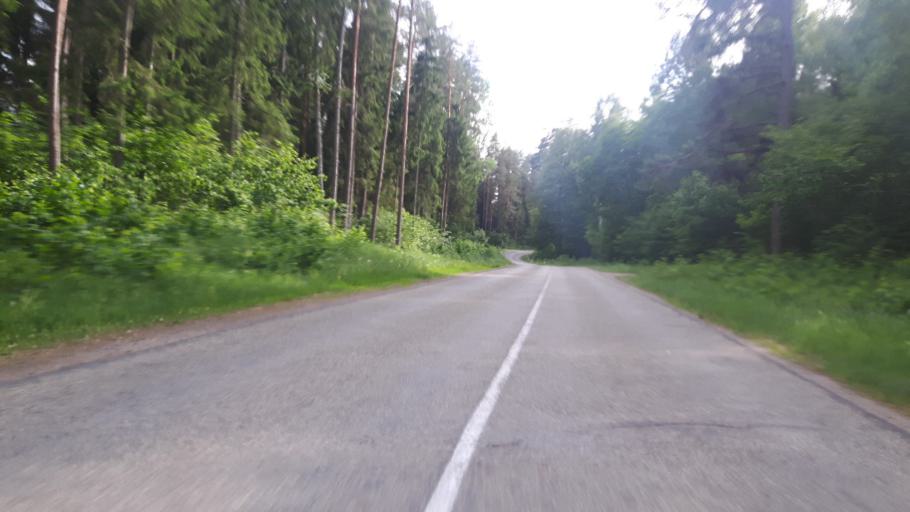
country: LV
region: Engure
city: Smarde
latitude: 56.9936
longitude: 23.3146
